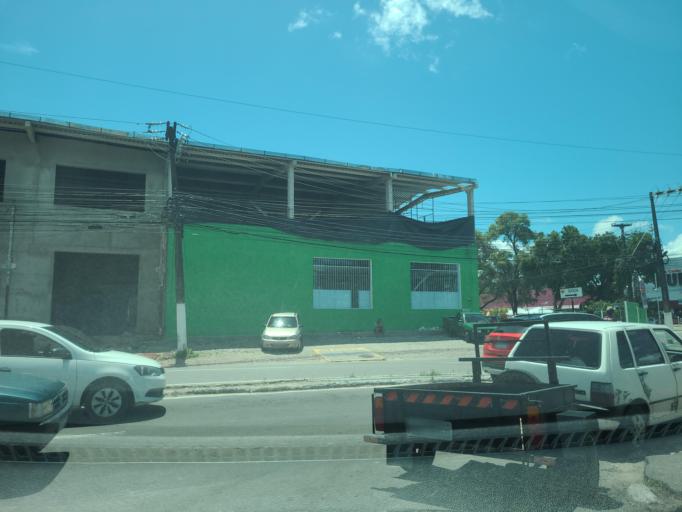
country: BR
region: Alagoas
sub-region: Maceio
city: Maceio
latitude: -9.5957
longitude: -35.7522
